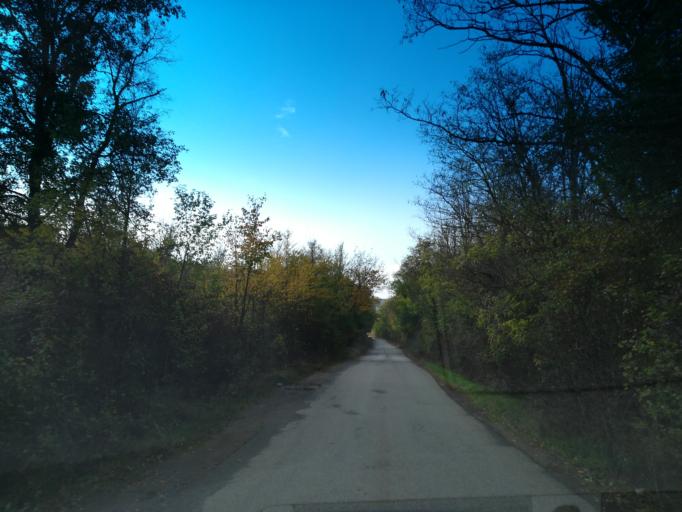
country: BG
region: Stara Zagora
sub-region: Obshtina Nikolaevo
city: Elkhovo
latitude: 42.3302
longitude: 25.4028
